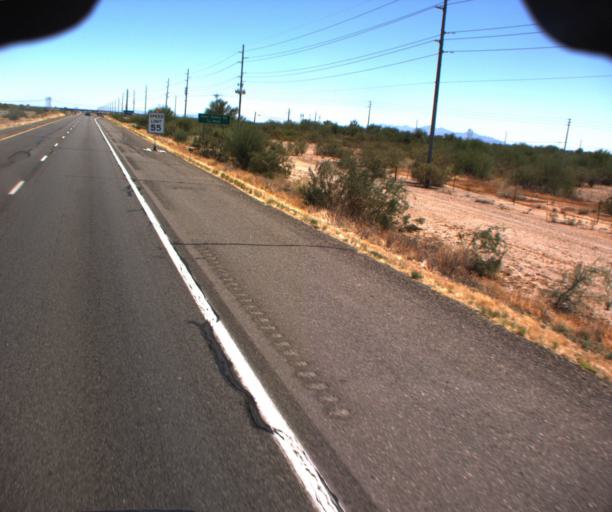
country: US
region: Arizona
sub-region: Maricopa County
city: Sun City West
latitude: 33.6985
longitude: -112.4271
